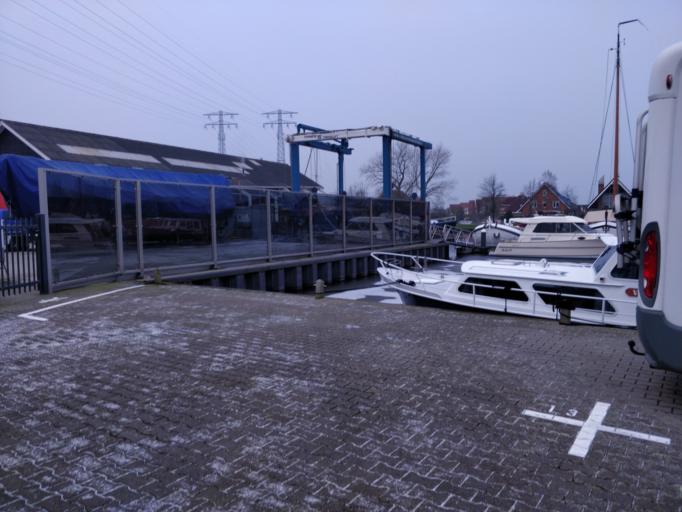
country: NL
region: Friesland
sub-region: Gemeente Leeuwarden
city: Camminghaburen
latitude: 53.1845
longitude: 5.8372
